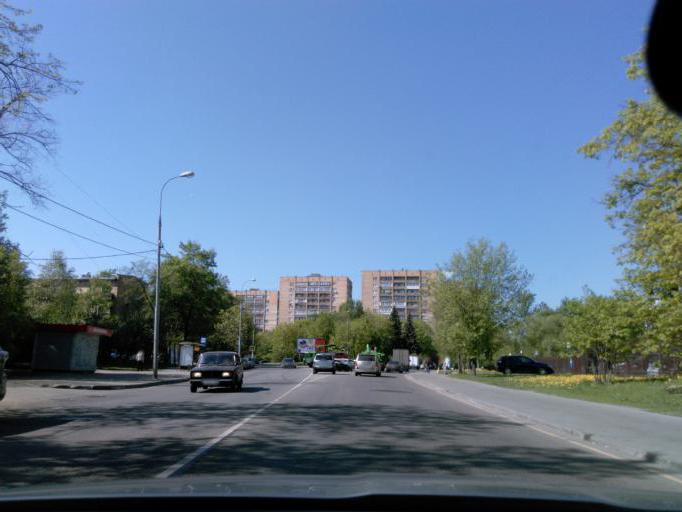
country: RU
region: Moscow
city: Golovinskiy
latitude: 55.8511
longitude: 37.4928
